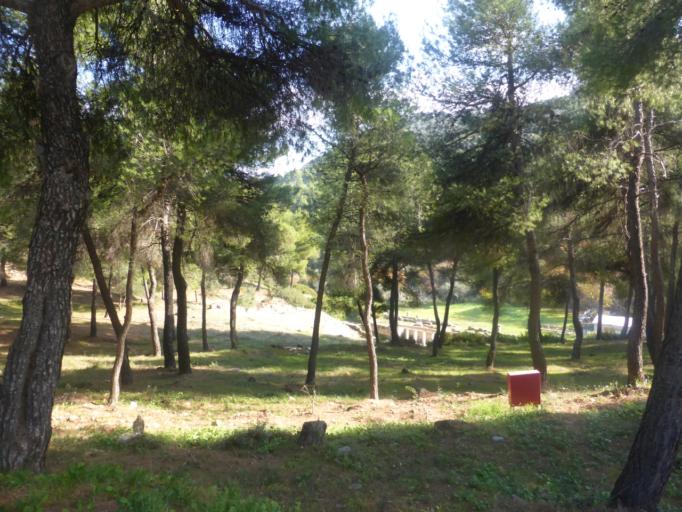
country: GR
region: Attica
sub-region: Nomarchia Anatolikis Attikis
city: Markopoulo Oropou
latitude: 38.2925
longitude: 23.8451
